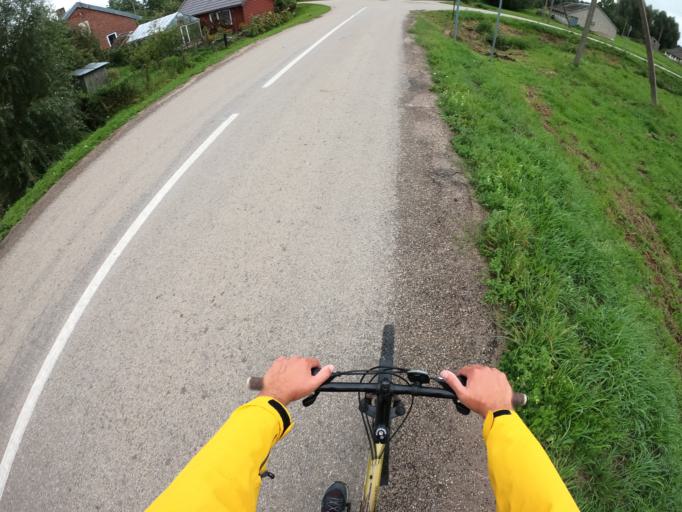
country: LT
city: Rusne
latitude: 55.3431
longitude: 21.3206
